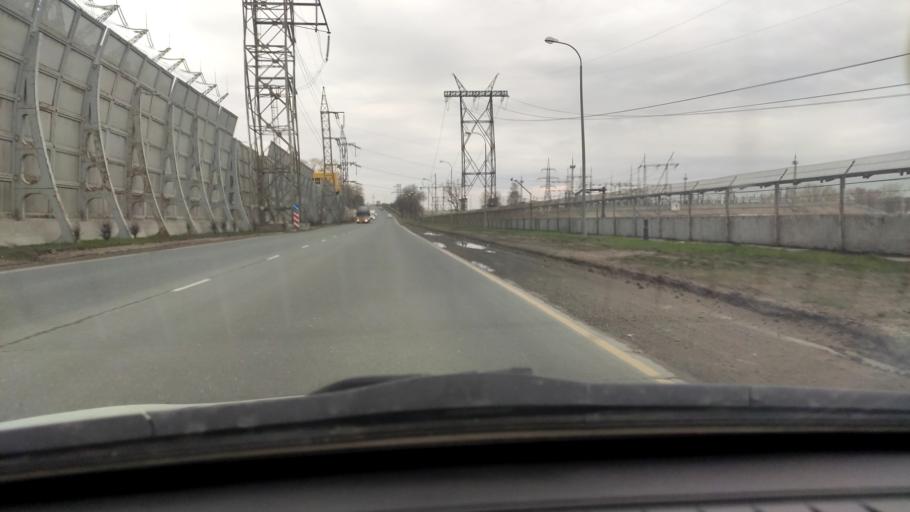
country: RU
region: Samara
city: Zhigulevsk
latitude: 53.4267
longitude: 49.4803
